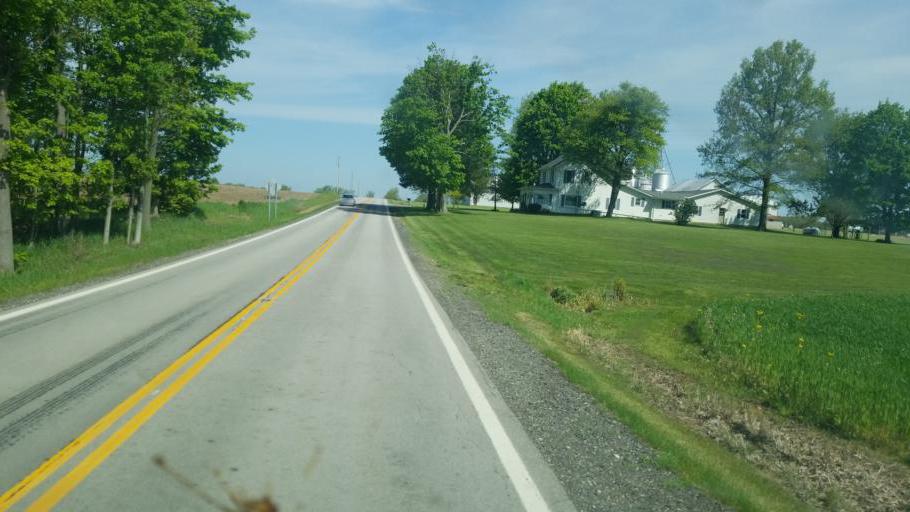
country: US
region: Ohio
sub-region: Seneca County
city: Tiffin
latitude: 40.9805
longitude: -83.0859
